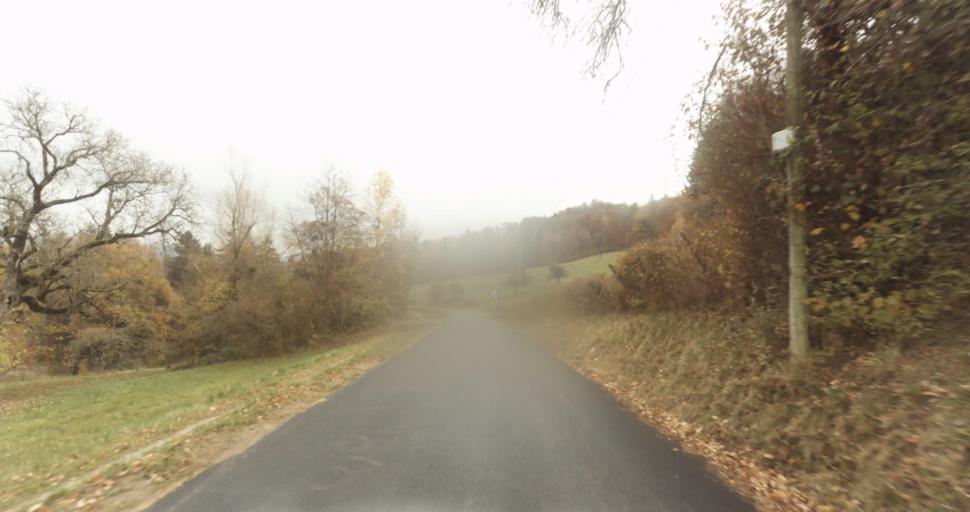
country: FR
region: Rhone-Alpes
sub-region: Departement de la Haute-Savoie
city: Saint-Martin-Bellevue
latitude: 45.9871
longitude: 6.1498
